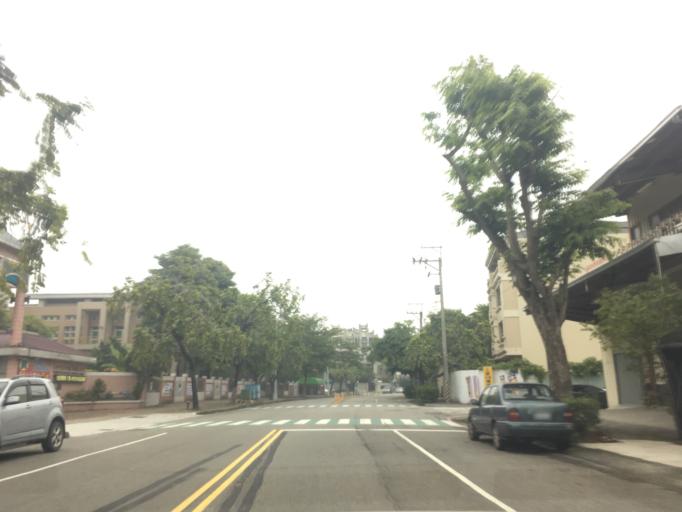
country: TW
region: Taiwan
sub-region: Taichung City
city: Taichung
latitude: 24.1934
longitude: 120.6767
